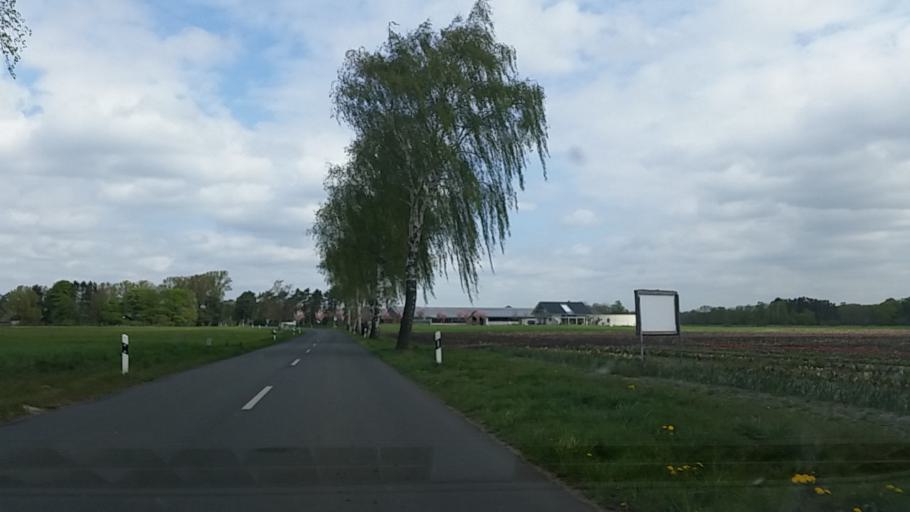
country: DE
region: Lower Saxony
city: Konigsmoor
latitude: 53.2142
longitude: 9.7145
